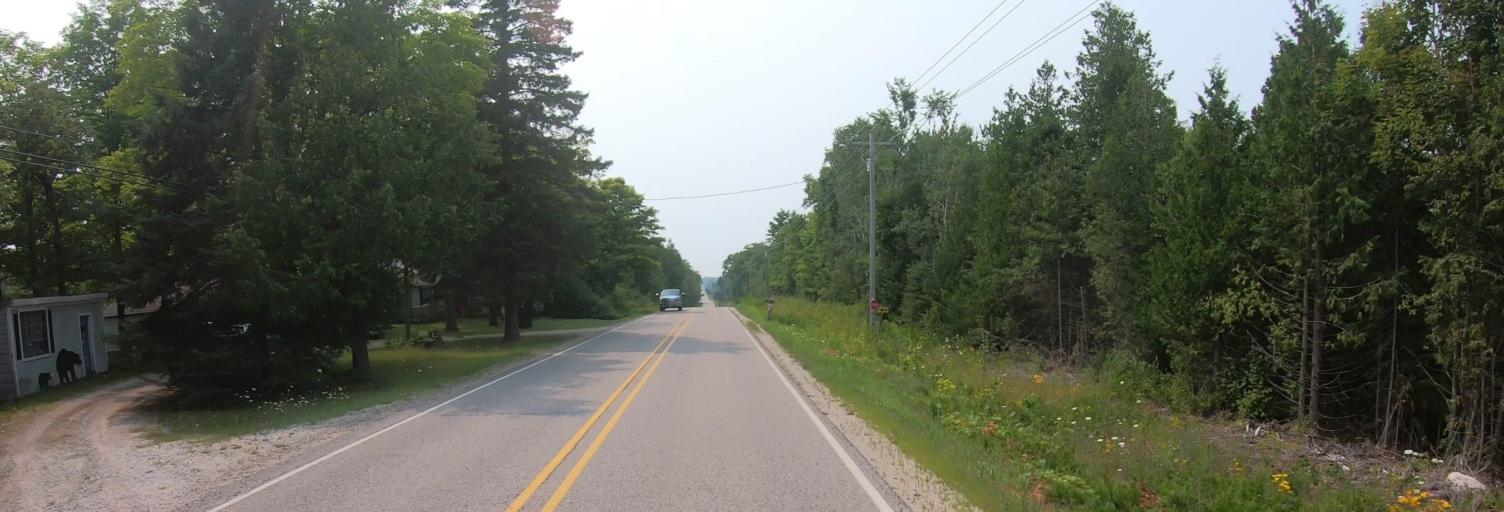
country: CA
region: Ontario
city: Thessalon
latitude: 46.0002
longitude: -83.9516
